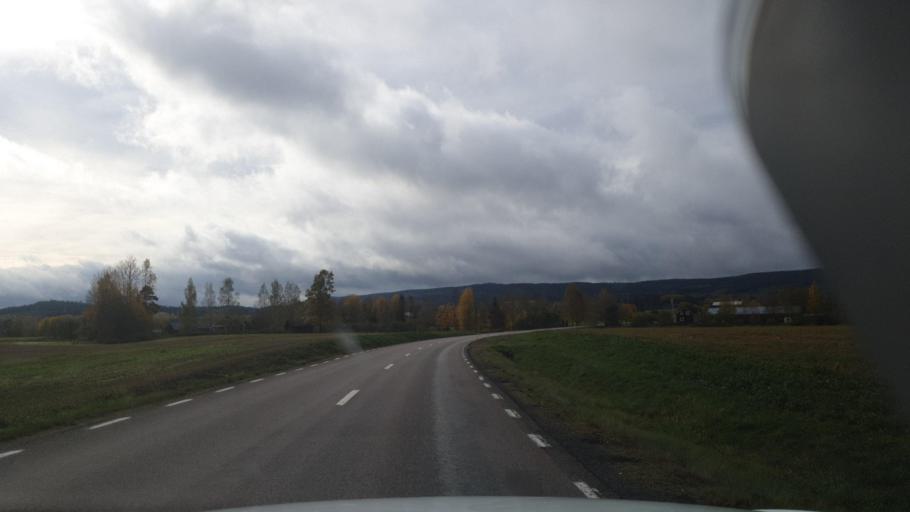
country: SE
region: Vaermland
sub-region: Sunne Kommun
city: Sunne
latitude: 59.7326
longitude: 13.1285
